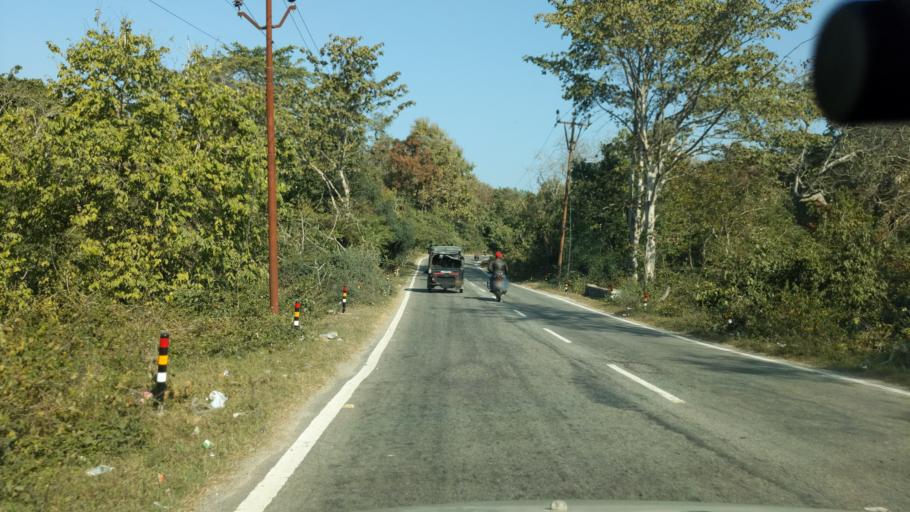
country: IN
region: Uttarakhand
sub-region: Naini Tal
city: Ramnagar
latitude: 29.3786
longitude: 79.1431
